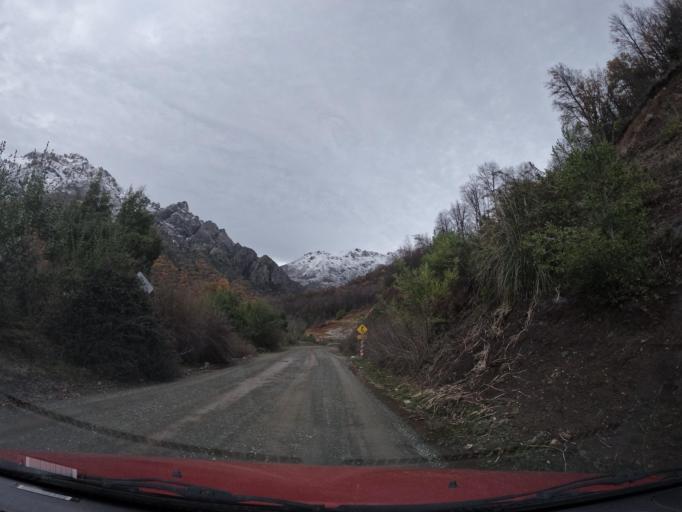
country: CL
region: Maule
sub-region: Provincia de Linares
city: Colbun
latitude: -35.8604
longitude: -71.1317
